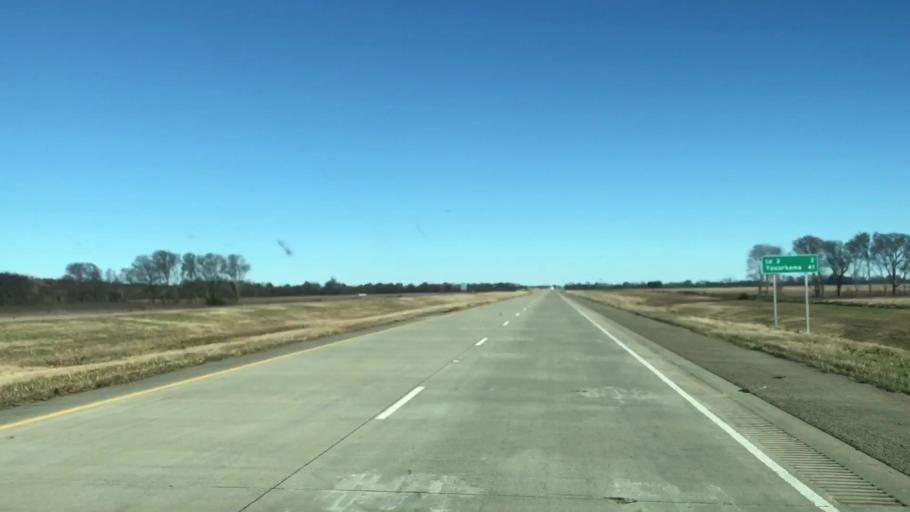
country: US
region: Louisiana
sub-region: Caddo Parish
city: Vivian
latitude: 32.8662
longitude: -93.8601
